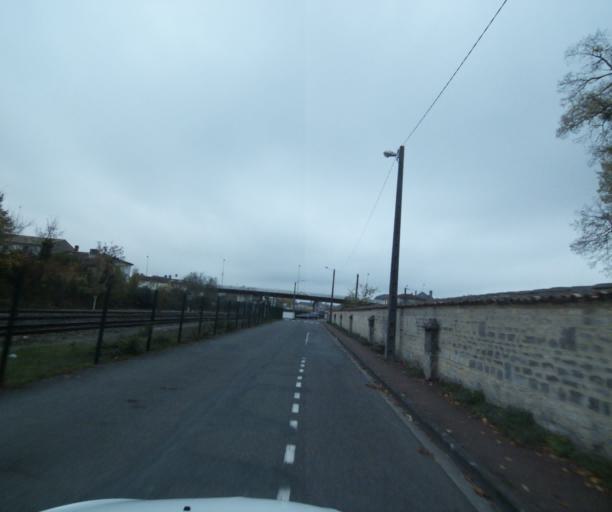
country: FR
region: Poitou-Charentes
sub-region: Departement de la Charente-Maritime
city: Saintes
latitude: 45.7445
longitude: -0.6182
